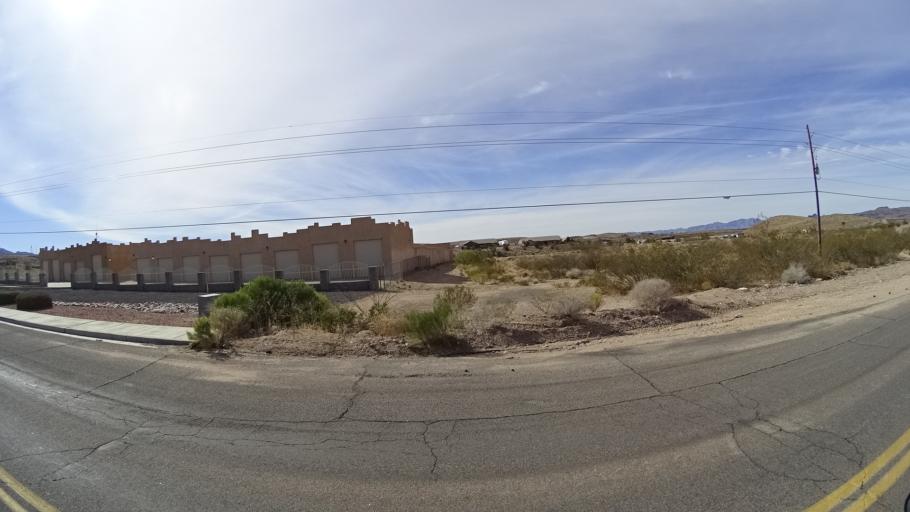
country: US
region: Arizona
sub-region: Mohave County
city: Kingman
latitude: 35.1807
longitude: -113.9962
